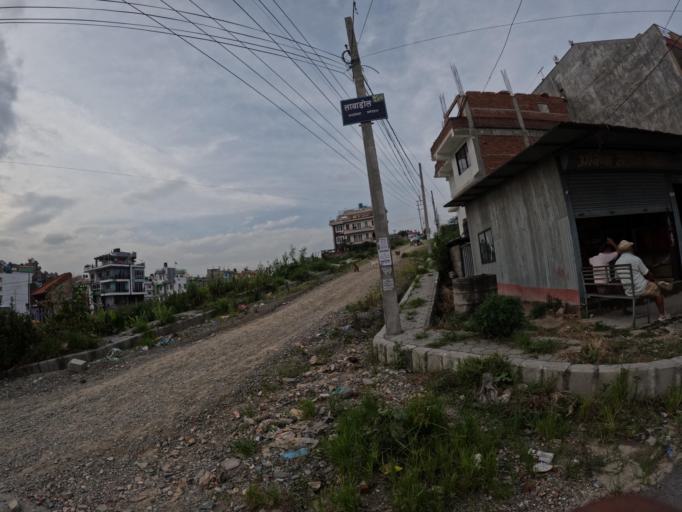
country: NP
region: Central Region
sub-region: Bagmati Zone
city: Bhaktapur
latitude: 27.6793
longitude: 85.3906
